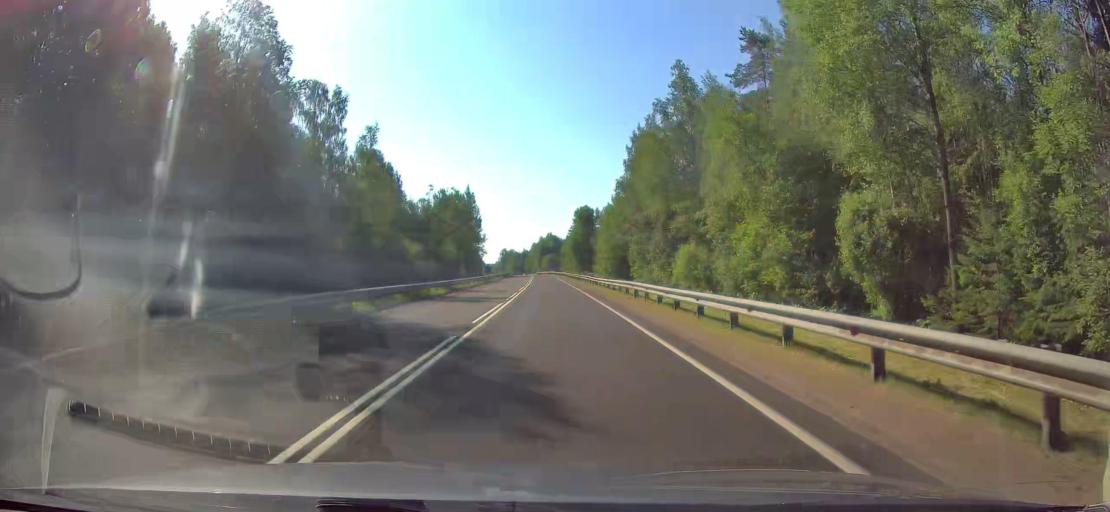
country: RU
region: Leningrad
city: Khvalovo
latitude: 59.8588
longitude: 32.8916
